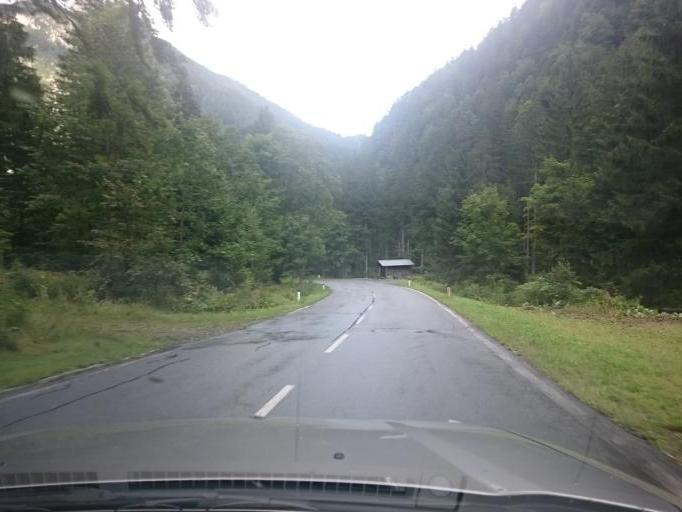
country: IT
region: Friuli Venezia Giulia
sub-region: Provincia di Udine
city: Ravascletto
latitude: 46.6233
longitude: 12.9414
